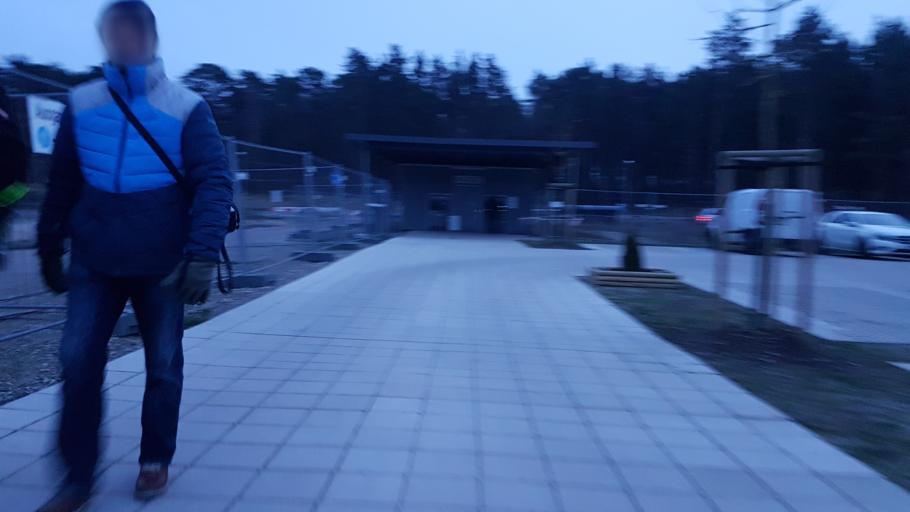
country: DE
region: Mecklenburg-Vorpommern
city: Ostseebad Binz
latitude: 54.4386
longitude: 13.5715
